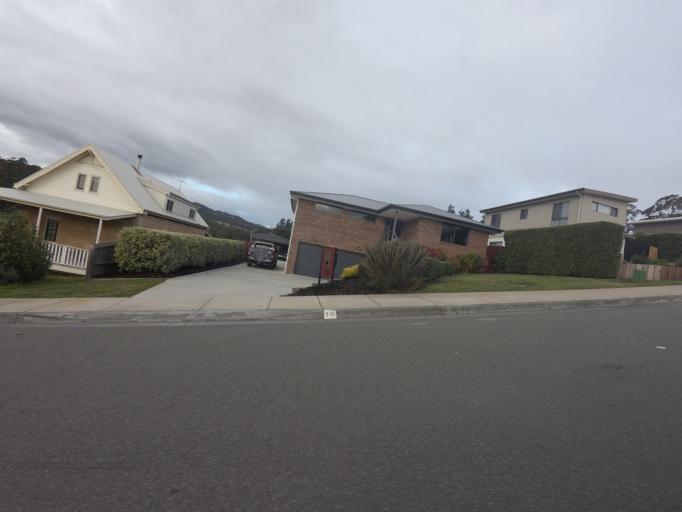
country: AU
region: Tasmania
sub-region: Clarence
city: Warrane
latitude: -42.8591
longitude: 147.4107
